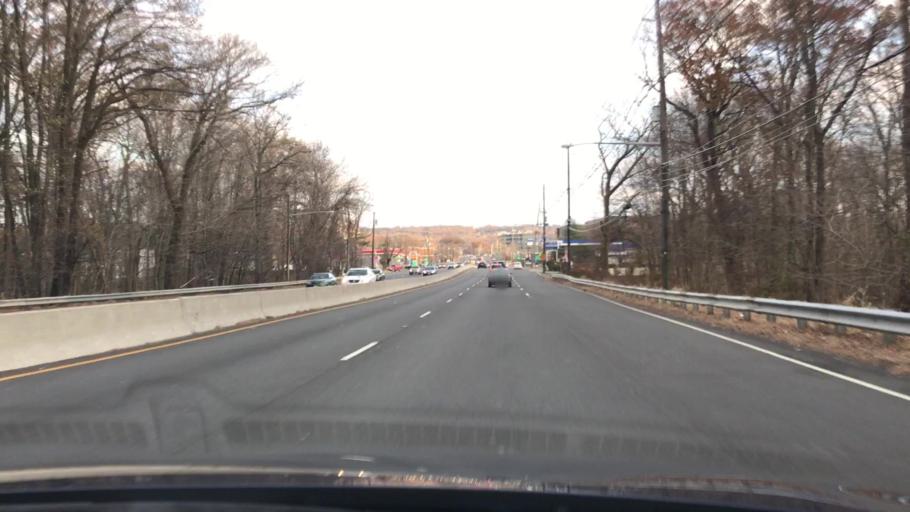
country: US
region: New Jersey
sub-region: Bergen County
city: Englewood
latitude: 40.8848
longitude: -73.9907
